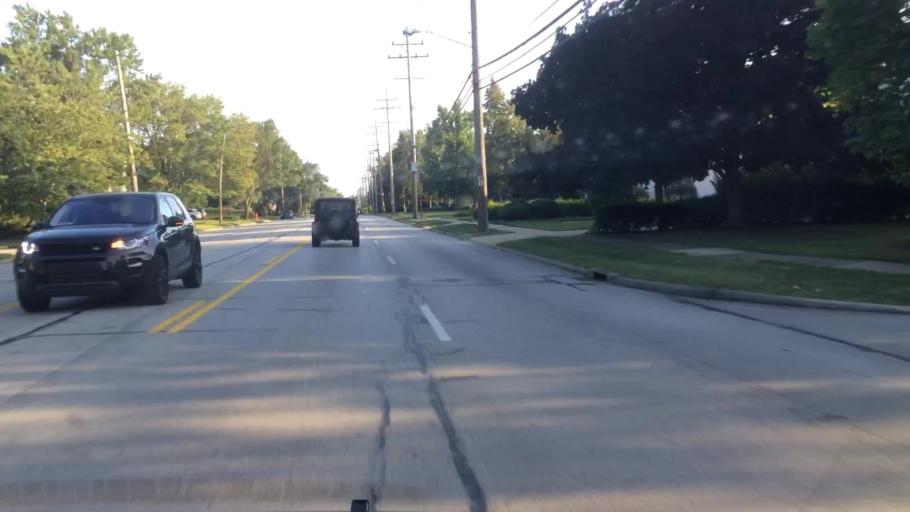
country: US
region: Ohio
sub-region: Cuyahoga County
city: Lyndhurst
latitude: 41.5321
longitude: -81.4972
